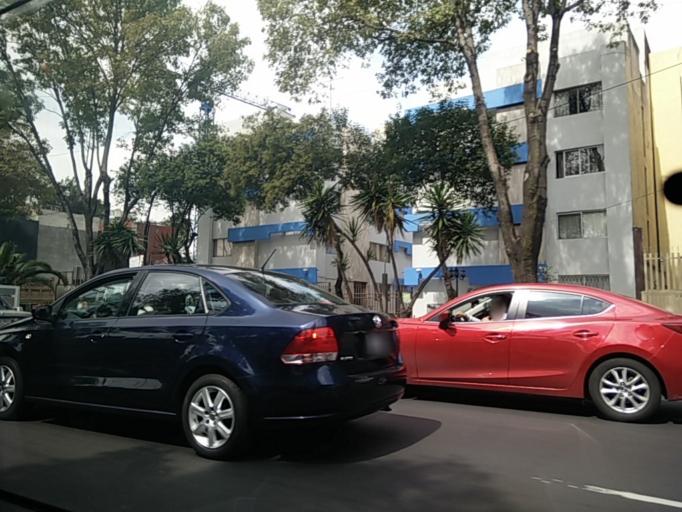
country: MX
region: Mexico City
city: Coyoacan
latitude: 19.3632
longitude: -99.1628
